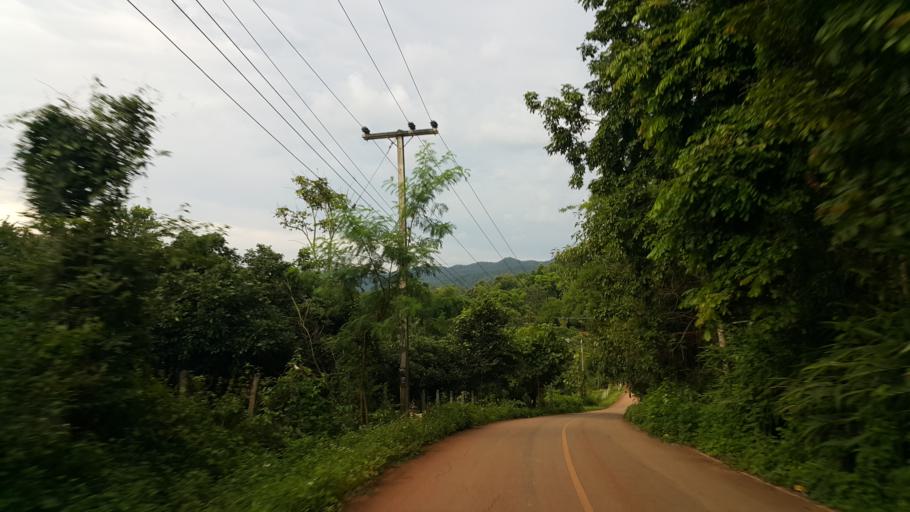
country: TH
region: Chiang Mai
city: Mae On
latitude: 18.8989
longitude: 99.2361
